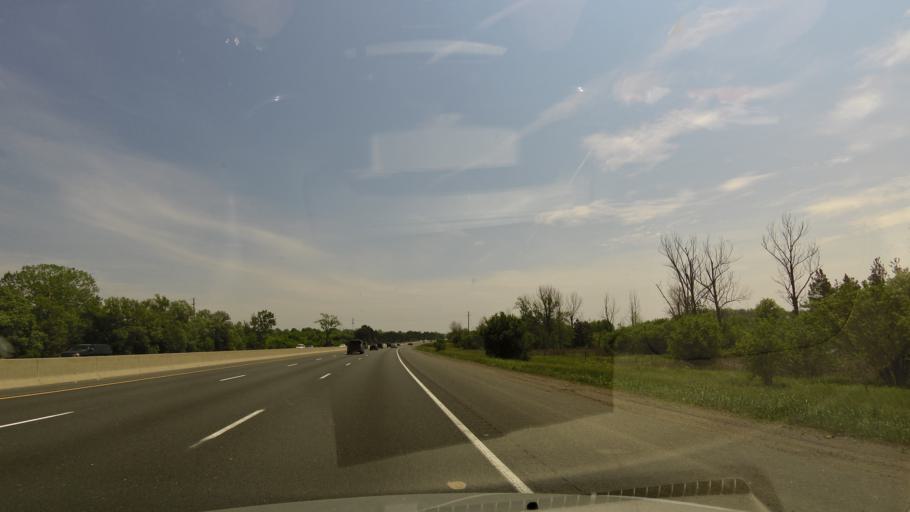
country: CA
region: Ontario
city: Oshawa
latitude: 43.8857
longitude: -78.8171
